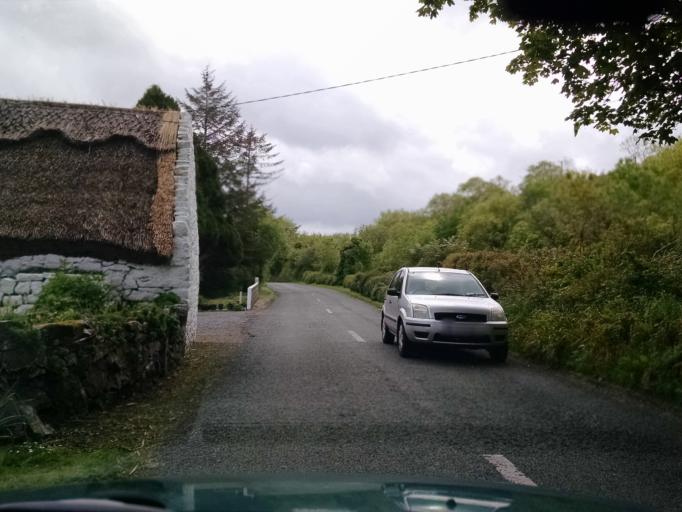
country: IE
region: Connaught
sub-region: County Galway
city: Bearna
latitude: 53.1294
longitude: -9.1856
